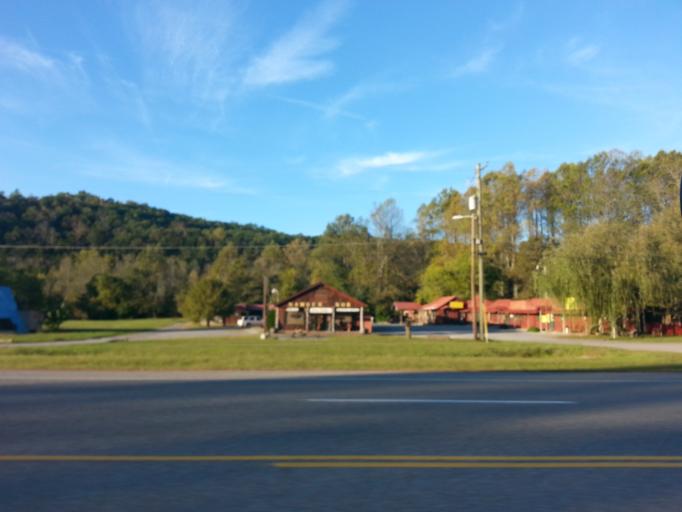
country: US
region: Tennessee
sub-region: Blount County
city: Wildwood
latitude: 35.6796
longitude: -83.7708
